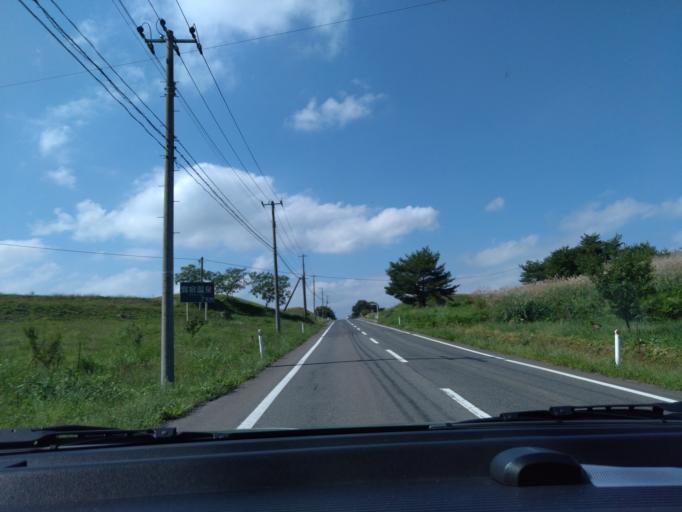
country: JP
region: Iwate
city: Shizukuishi
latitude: 39.6594
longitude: 140.9890
